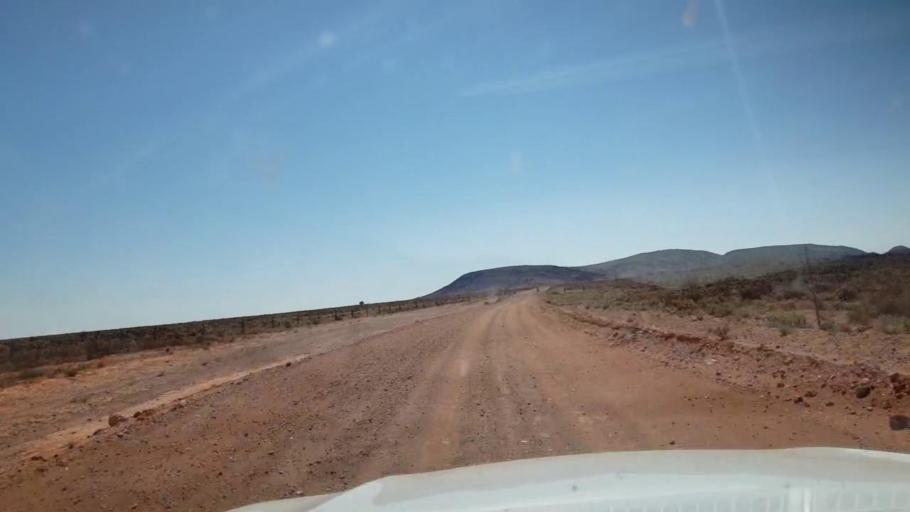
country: AU
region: South Australia
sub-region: Whyalla
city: Whyalla
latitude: -32.7097
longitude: 137.1395
